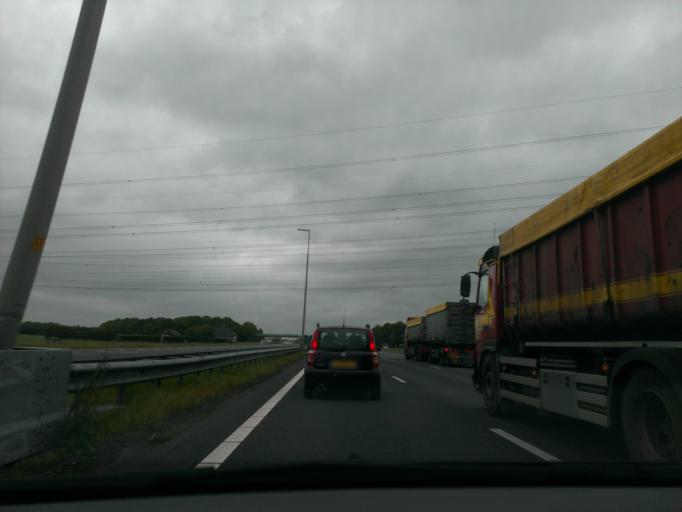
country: NL
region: Overijssel
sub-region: Gemeente Zwolle
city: Zwolle
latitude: 52.5404
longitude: 6.1649
